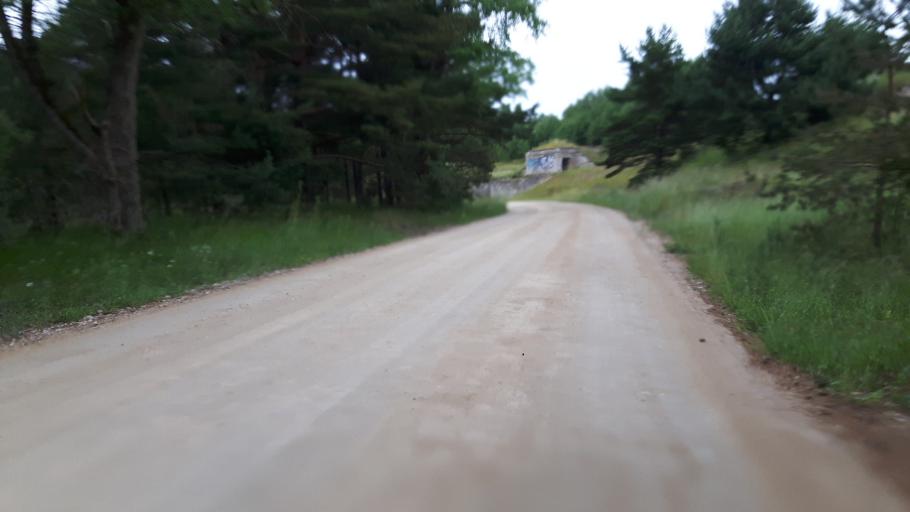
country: LV
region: Liepaja
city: Vec-Liepaja
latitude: 56.5902
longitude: 21.0241
